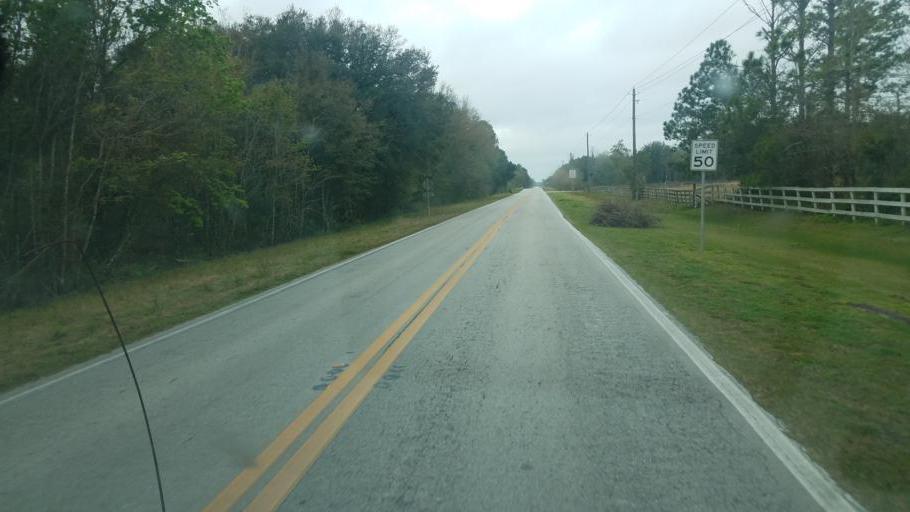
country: US
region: Florida
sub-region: Polk County
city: Polk City
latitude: 28.2590
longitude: -81.9233
